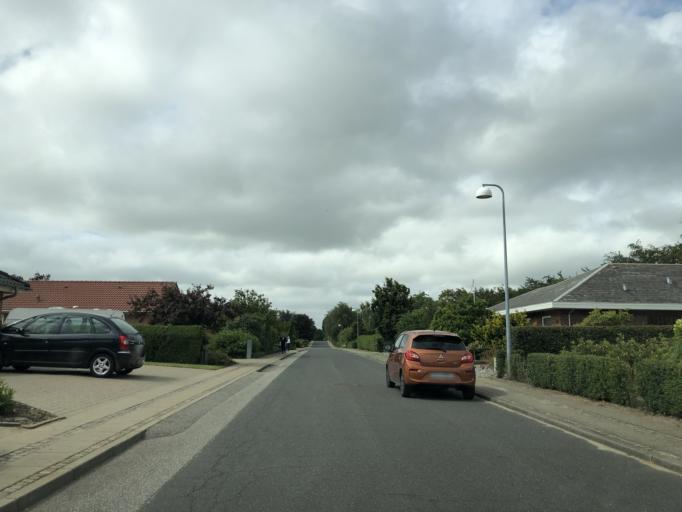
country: DK
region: Central Jutland
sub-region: Ringkobing-Skjern Kommune
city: Videbaek
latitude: 56.2002
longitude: 8.5729
